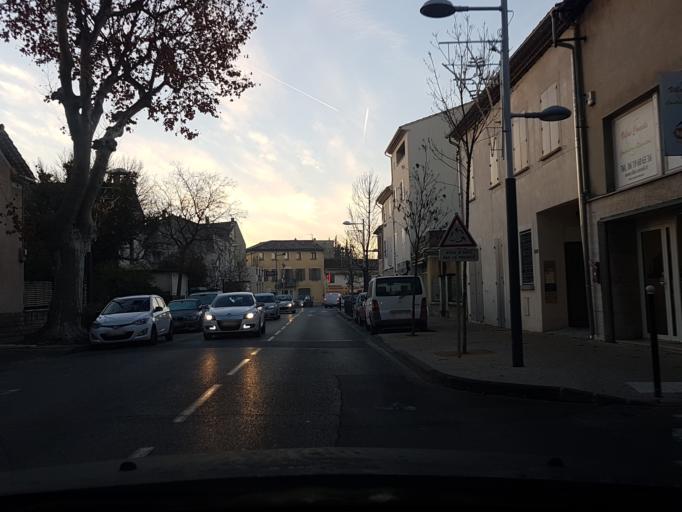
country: FR
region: Provence-Alpes-Cote d'Azur
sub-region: Departement du Vaucluse
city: Monteux
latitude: 44.0357
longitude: 4.9992
